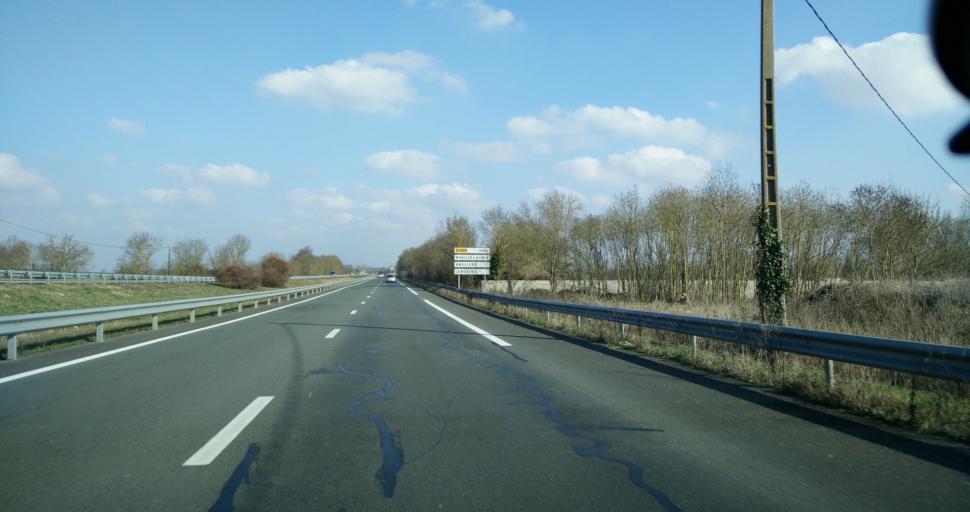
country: FR
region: Poitou-Charentes
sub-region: Departement de la Charente-Maritime
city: Verines
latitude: 46.2223
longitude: -0.9621
